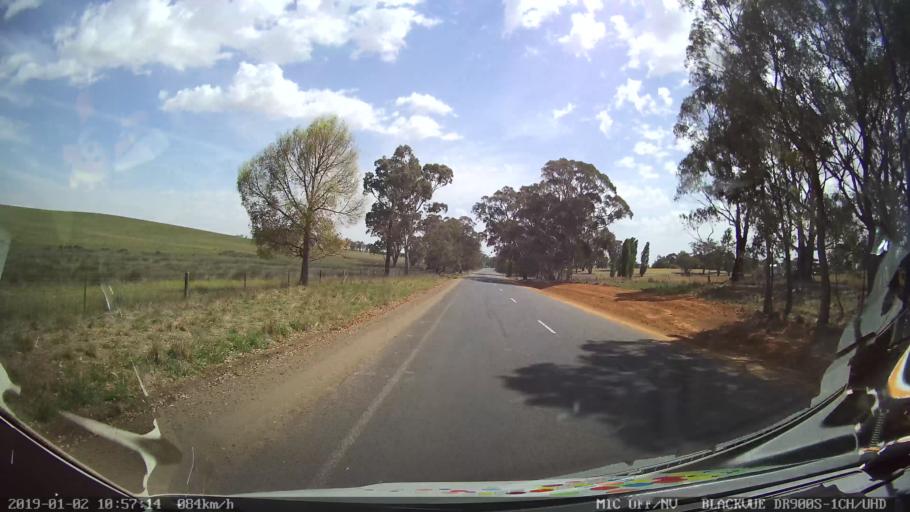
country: AU
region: New South Wales
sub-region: Cootamundra
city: Cootamundra
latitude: -34.6378
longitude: 148.2814
